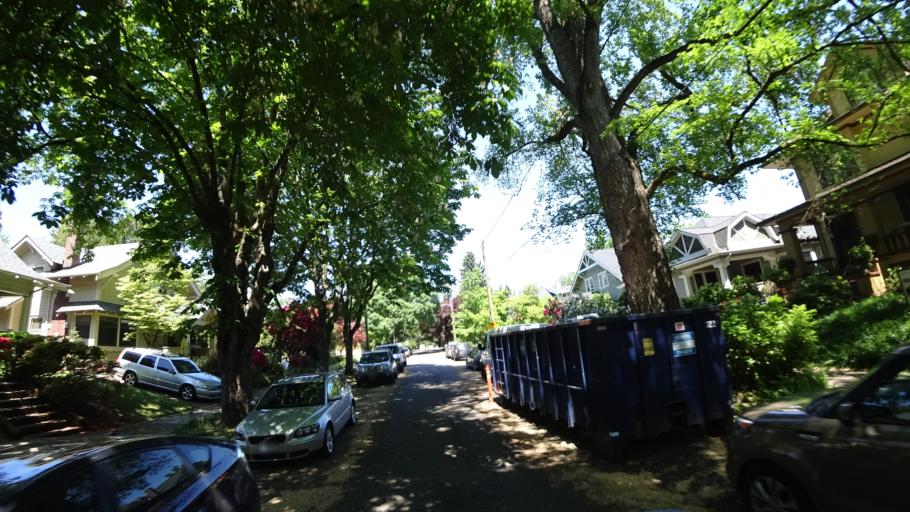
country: US
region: Oregon
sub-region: Multnomah County
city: Portland
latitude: 45.5410
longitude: -122.6474
